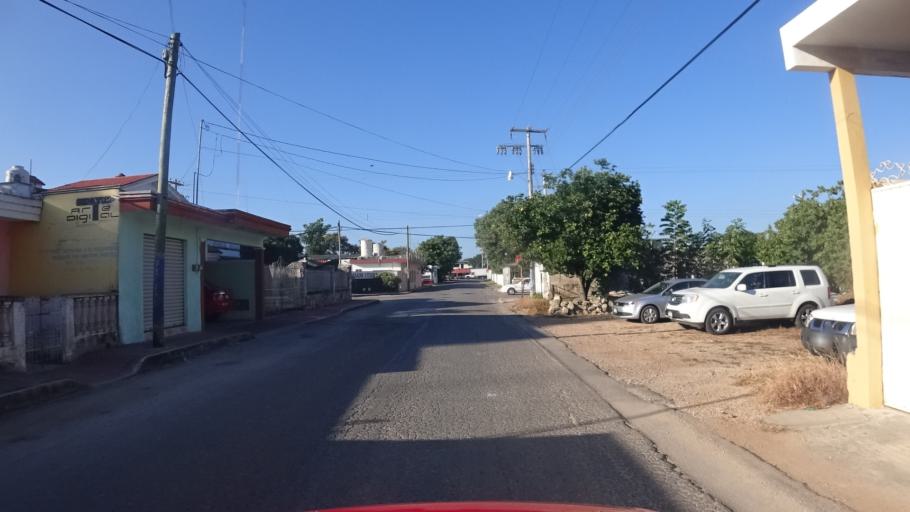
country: MX
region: Yucatan
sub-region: Tizimin
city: Tizimin
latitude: 21.1515
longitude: -88.1635
